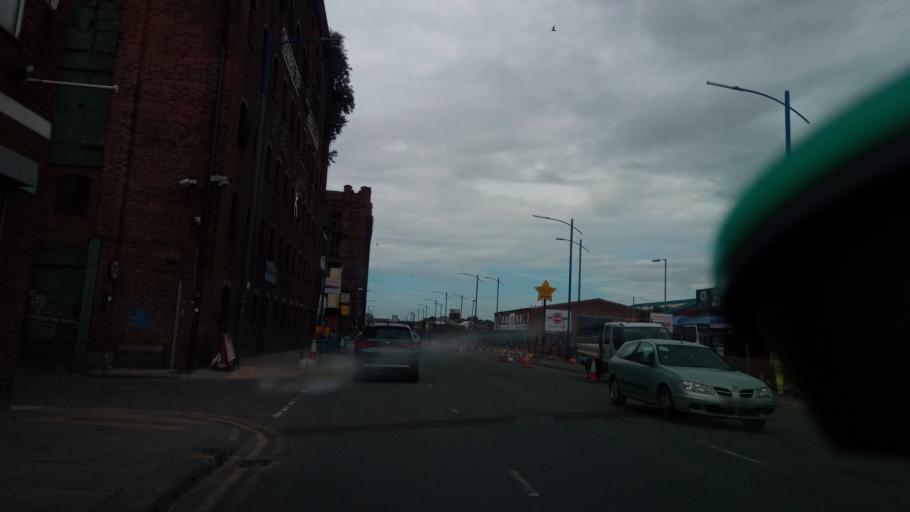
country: GB
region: England
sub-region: Liverpool
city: Liverpool
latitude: 53.4193
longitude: -2.9967
